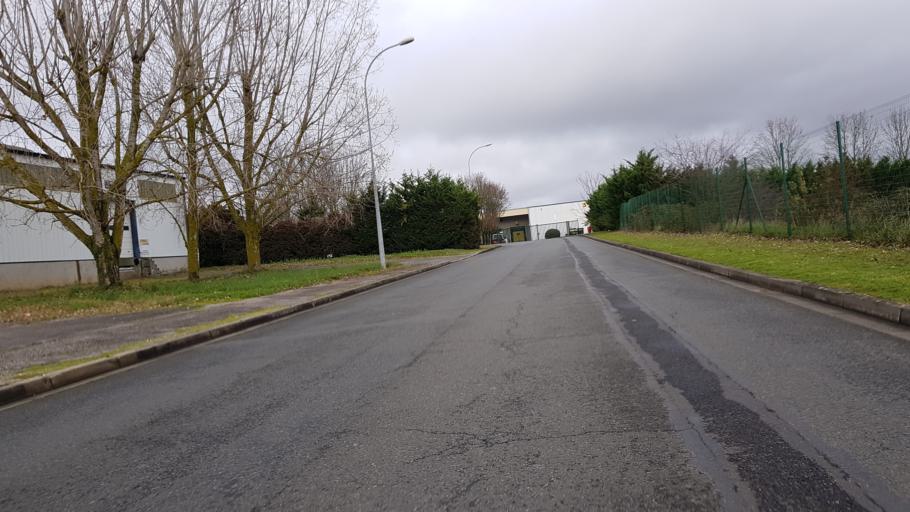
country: FR
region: Poitou-Charentes
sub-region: Departement de la Vienne
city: Chasseneuil-du-Poitou
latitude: 46.6583
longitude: 0.3725
